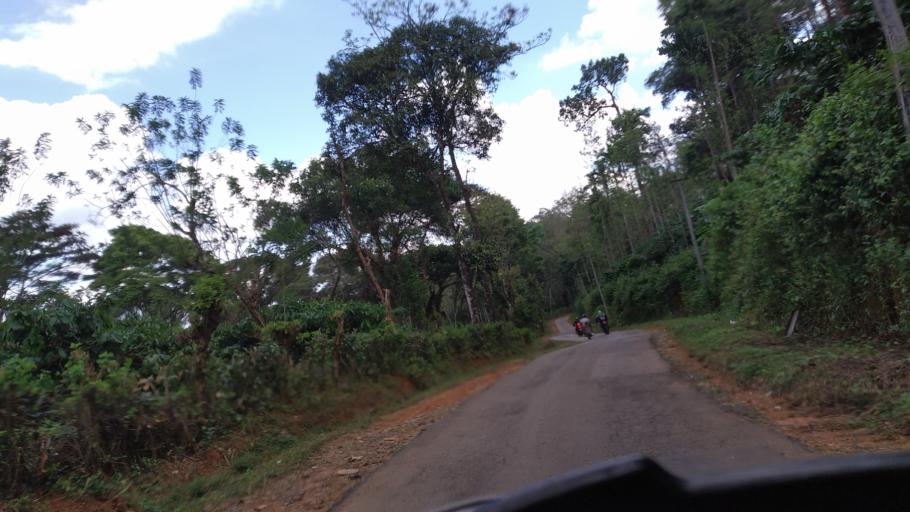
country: IN
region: Karnataka
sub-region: Kodagu
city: Ponnampet
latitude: 12.0377
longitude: 75.9082
